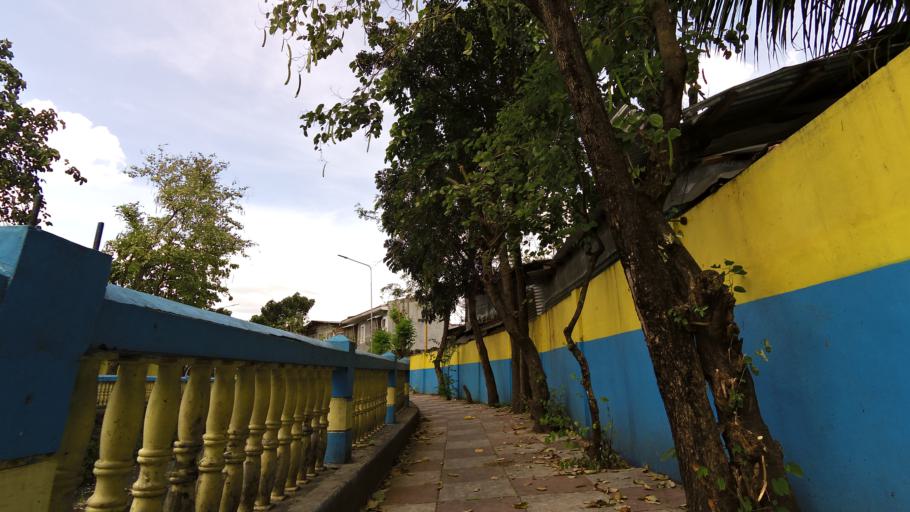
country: PH
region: Calabarzon
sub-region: Province of Rizal
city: Pateros
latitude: 14.5640
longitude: 121.0904
